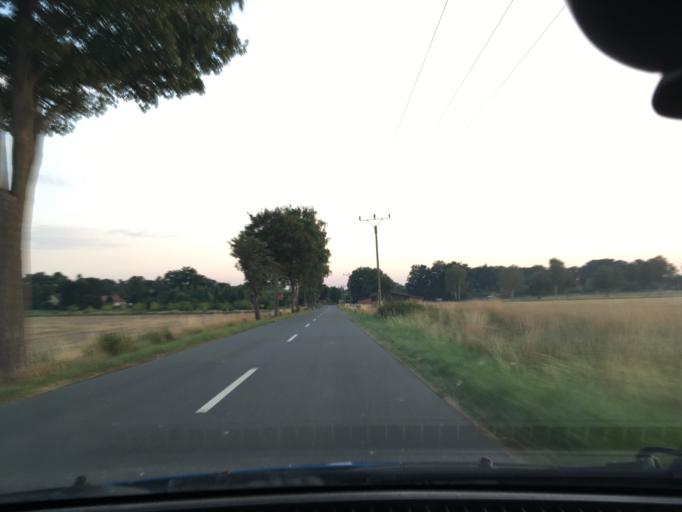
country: DE
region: Lower Saxony
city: Barnstedt
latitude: 53.0945
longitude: 10.4055
